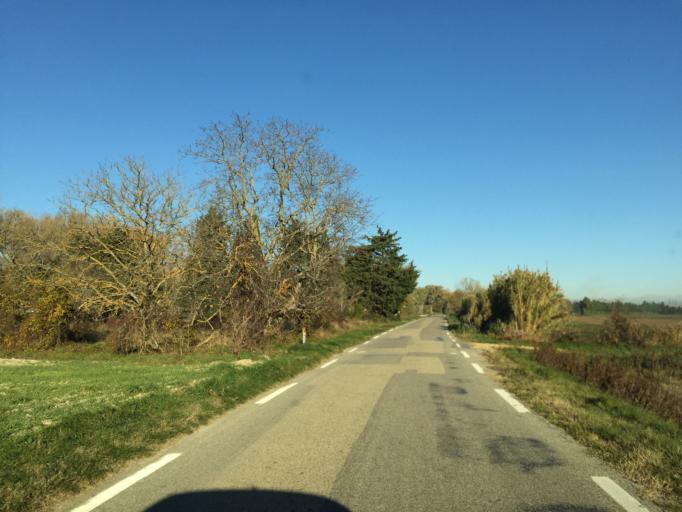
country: FR
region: Provence-Alpes-Cote d'Azur
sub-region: Departement du Vaucluse
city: Bedarrides
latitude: 44.0456
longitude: 4.9317
